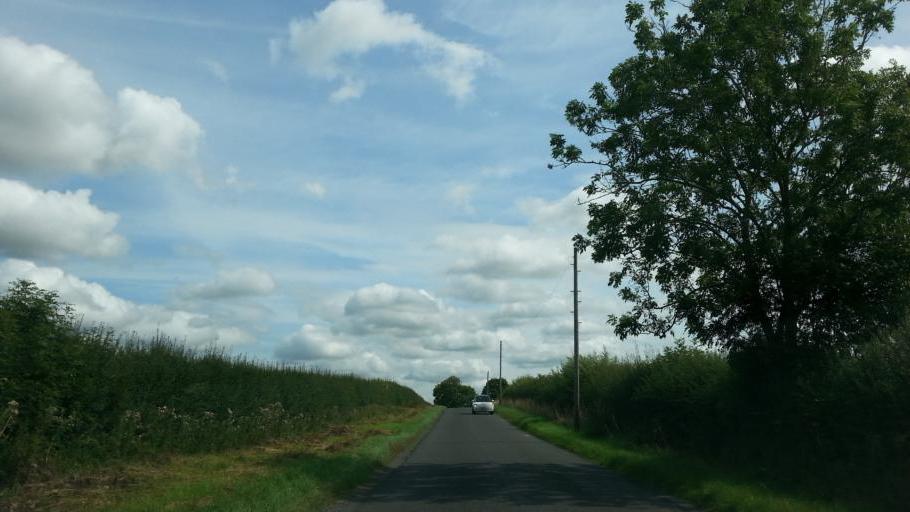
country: GB
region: England
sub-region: Leicestershire
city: Kibworth Harcourt
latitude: 52.5272
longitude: -1.0151
